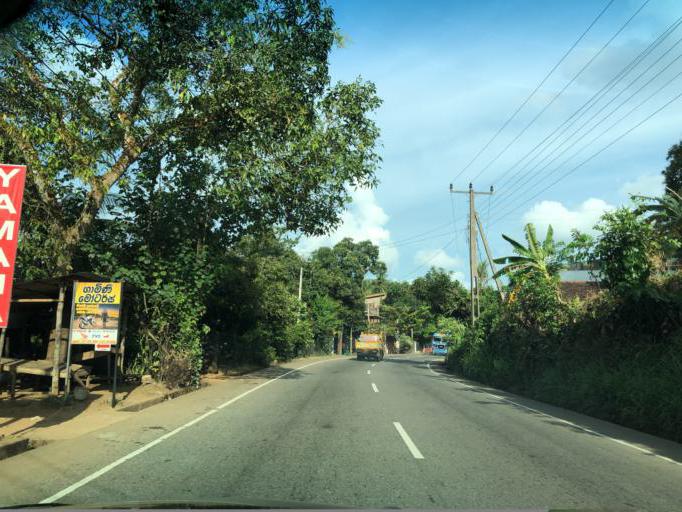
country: LK
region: Western
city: Horawala Junction
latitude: 6.5273
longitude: 80.1011
